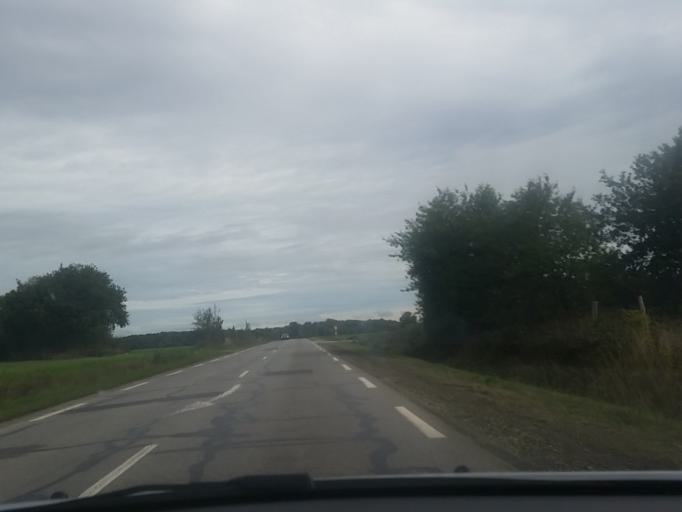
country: FR
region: Brittany
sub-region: Departement d'Ille-et-Vilaine
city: Martigne-Ferchaud
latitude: 47.7919
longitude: -1.3458
